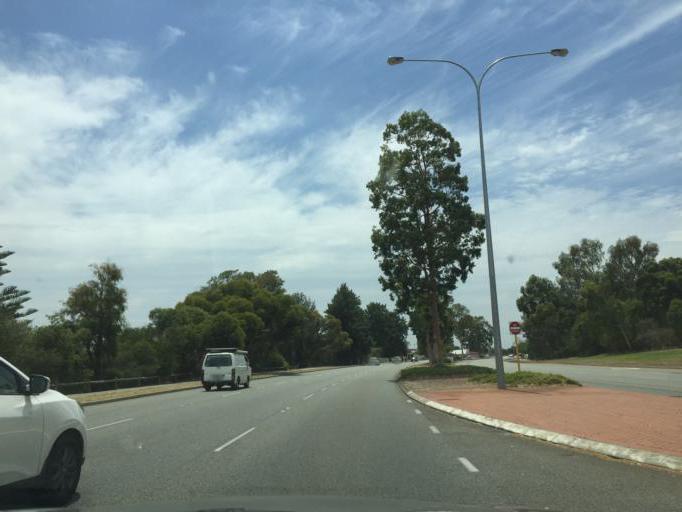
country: AU
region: Western Australia
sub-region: Melville
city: Winthrop
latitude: -32.0640
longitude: 115.8328
